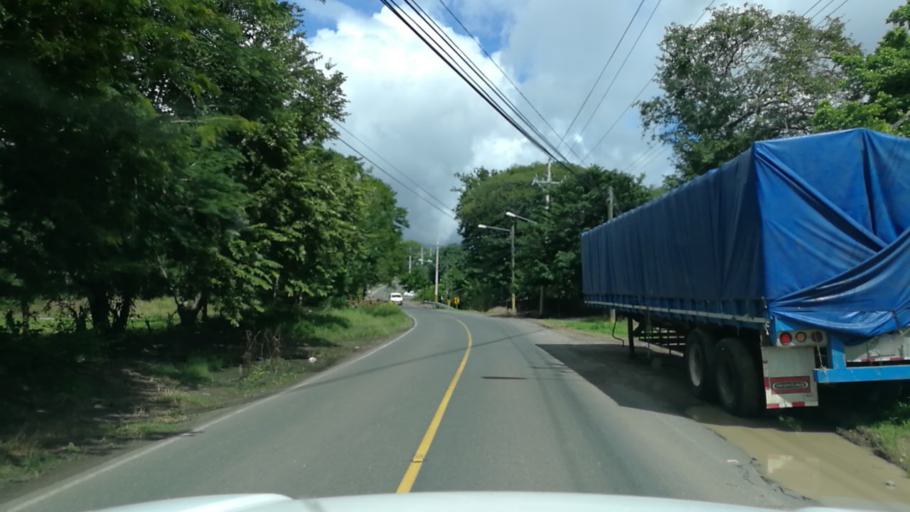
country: CR
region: Guanacaste
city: Bagaces
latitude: 10.5354
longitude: -85.2553
